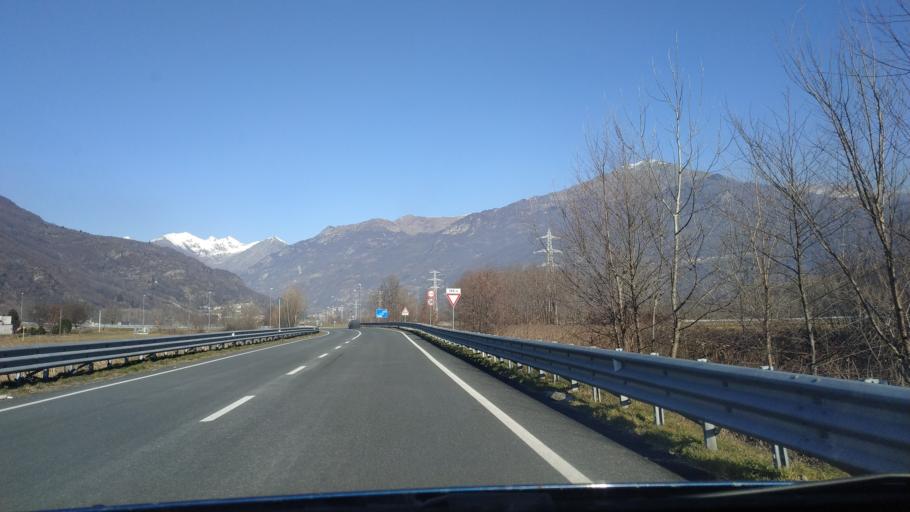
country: IT
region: Piedmont
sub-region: Provincia di Torino
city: Quassolo
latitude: 45.5062
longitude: 7.8356
